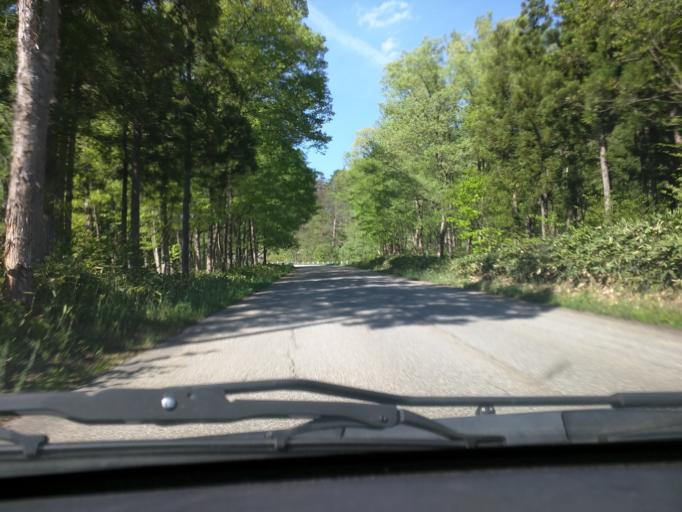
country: JP
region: Fukushima
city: Kitakata
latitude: 37.5701
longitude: 139.6354
